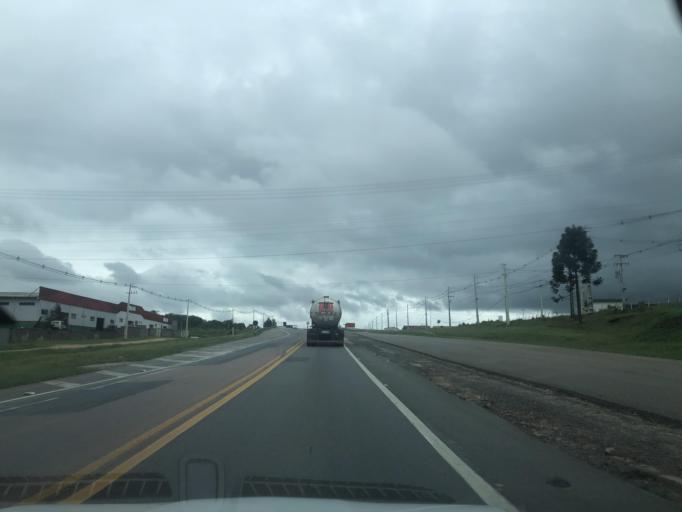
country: BR
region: Parana
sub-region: Araucaria
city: Araucaria
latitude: -25.7250
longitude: -49.3179
